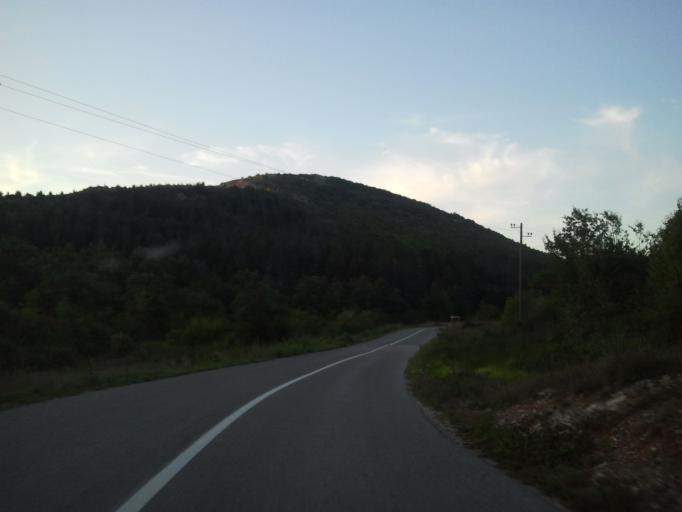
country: HR
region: Zadarska
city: Obrovac
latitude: 44.4273
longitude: 15.6600
